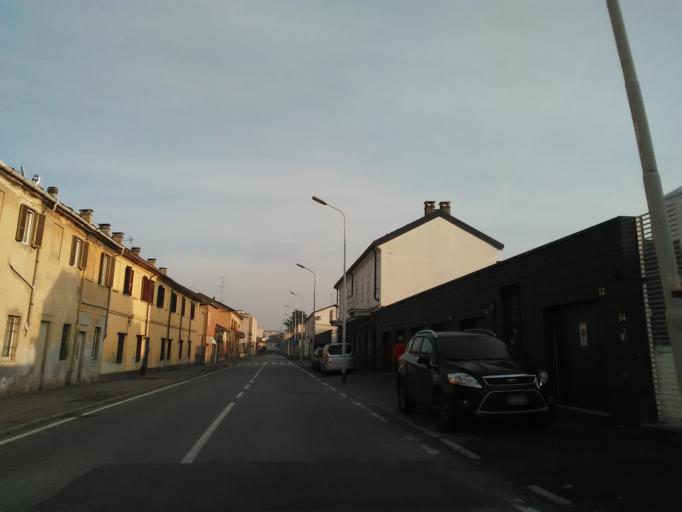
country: IT
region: Piedmont
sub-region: Provincia di Vercelli
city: Vercelli
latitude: 45.3296
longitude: 8.4061
